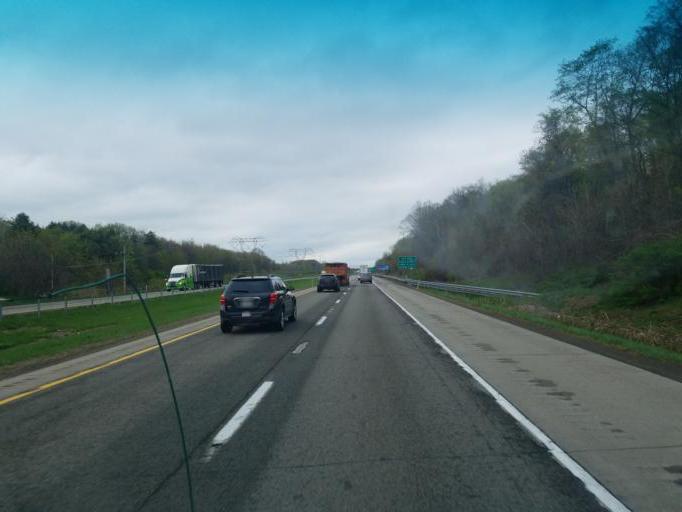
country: US
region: Pennsylvania
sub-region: Erie County
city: Erie
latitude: 42.0390
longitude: -80.1058
